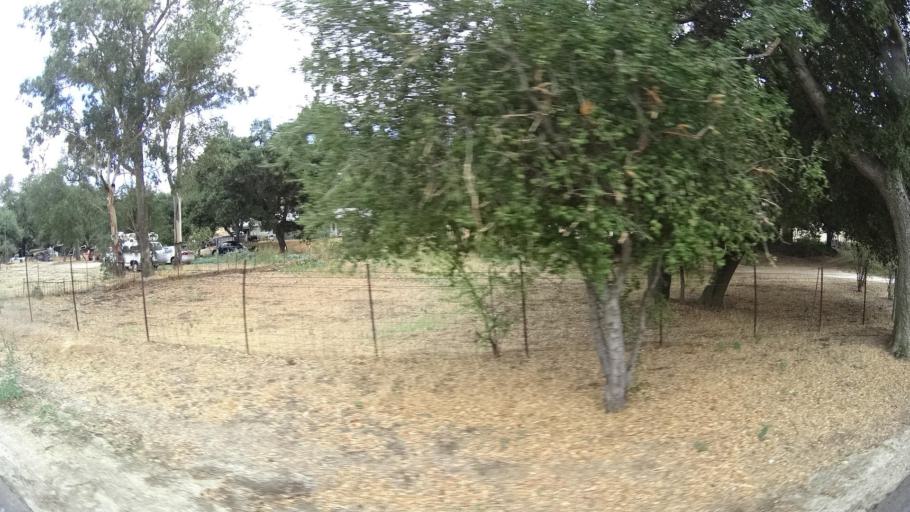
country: US
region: California
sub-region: San Diego County
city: Campo
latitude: 32.6584
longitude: -116.4984
